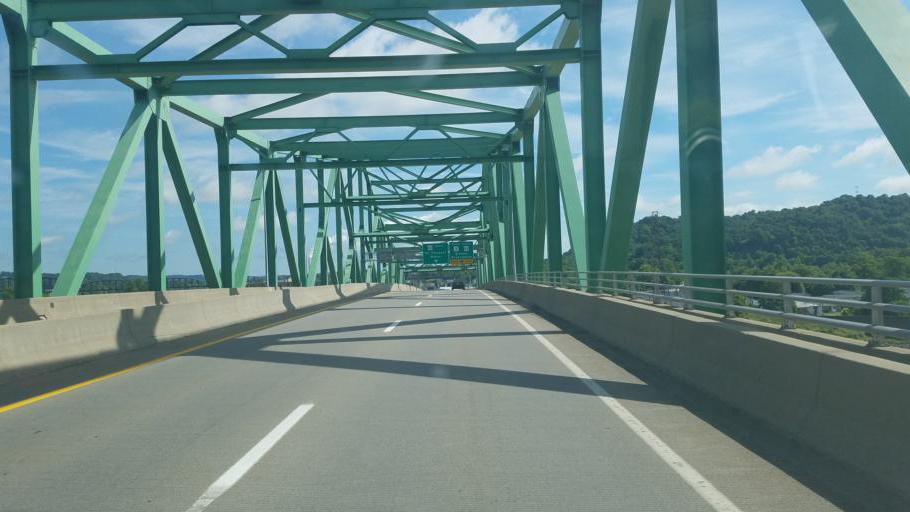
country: US
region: West Virginia
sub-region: Mason County
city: Point Pleasant
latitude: 38.8367
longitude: -82.1397
